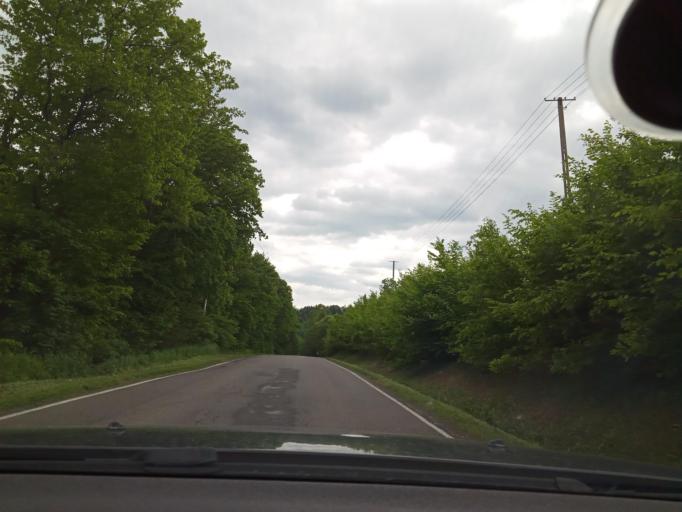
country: PL
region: Lesser Poland Voivodeship
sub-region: Powiat limanowski
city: Tymbark
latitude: 49.7534
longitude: 20.3464
